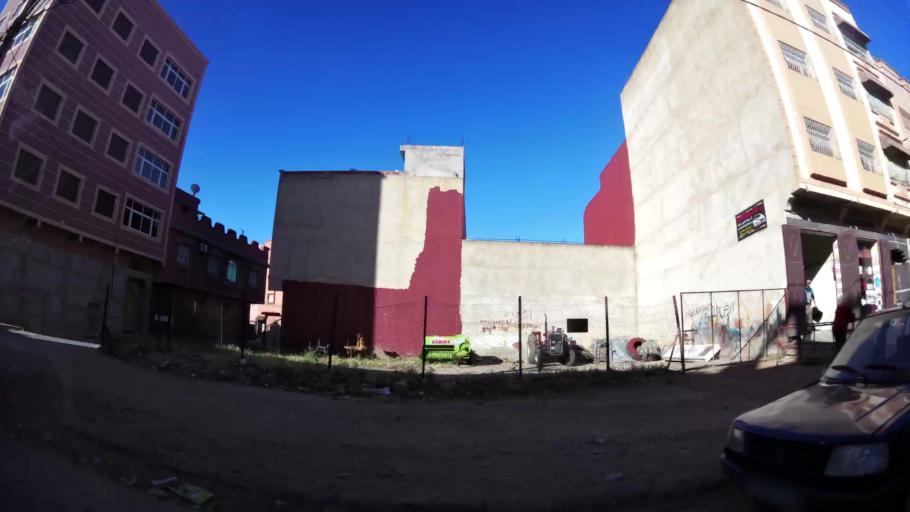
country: MA
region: Oriental
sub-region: Berkane-Taourirt
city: Berkane
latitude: 34.9305
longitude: -2.3416
